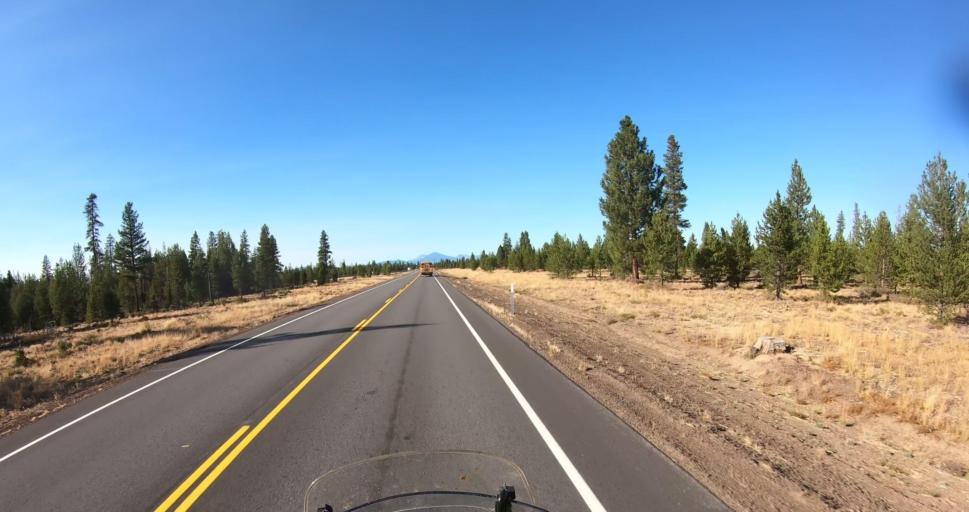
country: US
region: Oregon
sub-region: Deschutes County
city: La Pine
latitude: 43.6034
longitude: -121.4991
